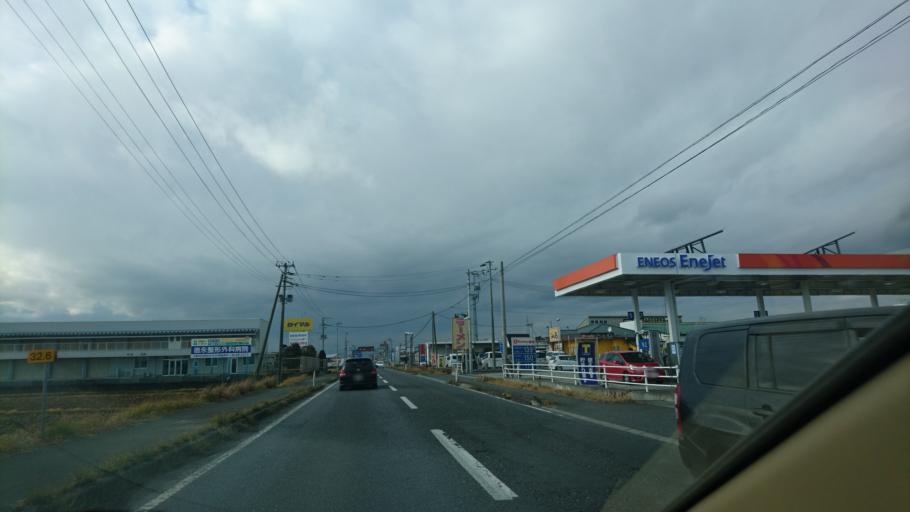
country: JP
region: Miyagi
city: Furukawa
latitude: 38.5675
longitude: 140.9973
